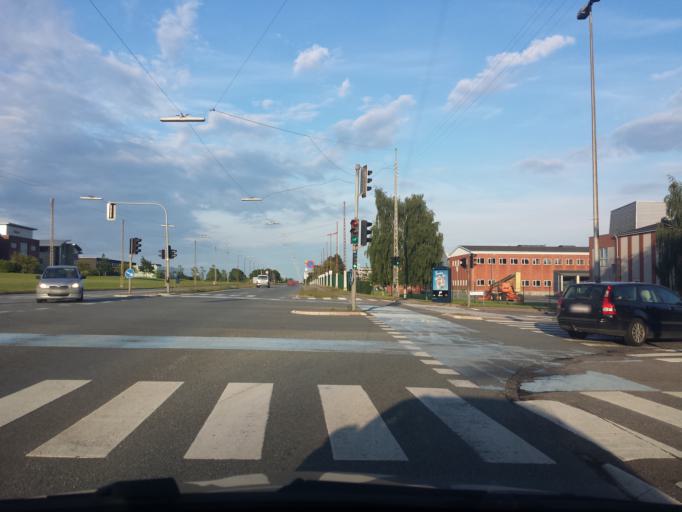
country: DK
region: Capital Region
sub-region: Ballerup Kommune
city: Ballerup
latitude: 55.7287
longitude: 12.3868
